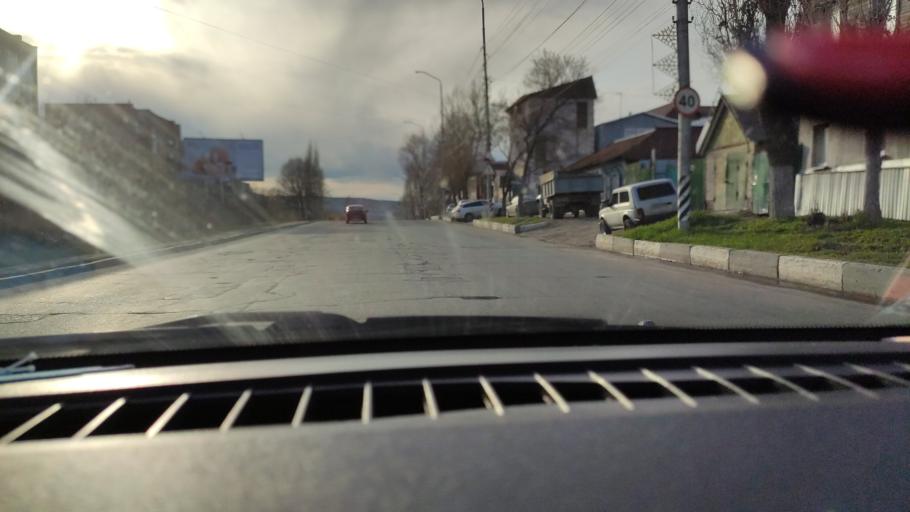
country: RU
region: Saratov
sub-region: Saratovskiy Rayon
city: Saratov
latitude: 51.5409
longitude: 46.0462
